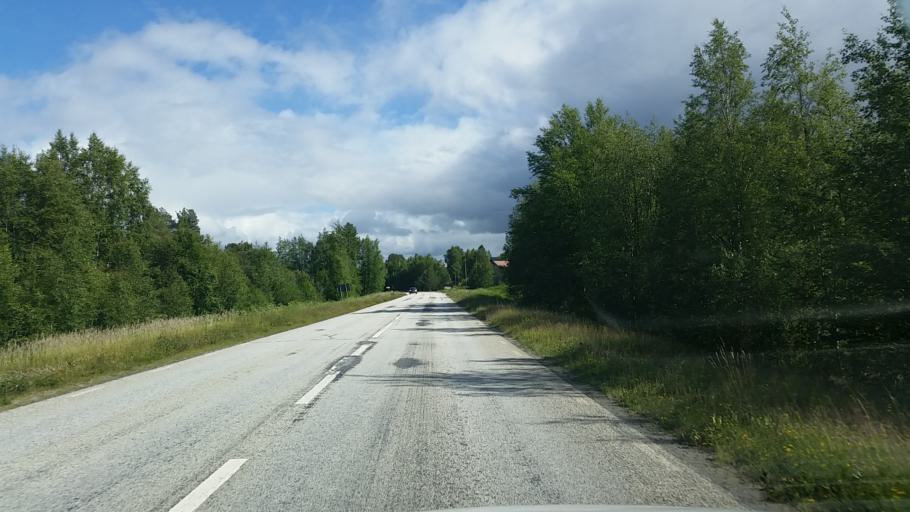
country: SE
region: Jaemtland
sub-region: Harjedalens Kommun
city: Sveg
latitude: 62.4105
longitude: 13.6834
